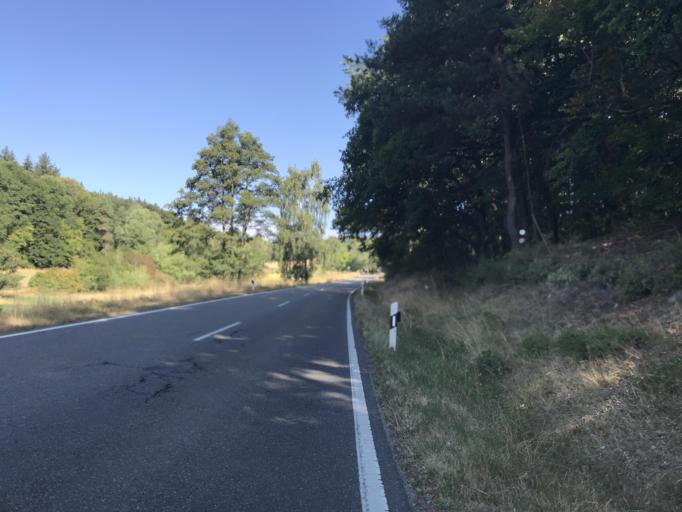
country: DE
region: Hesse
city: Geisenheim
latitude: 50.0185
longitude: 7.9651
